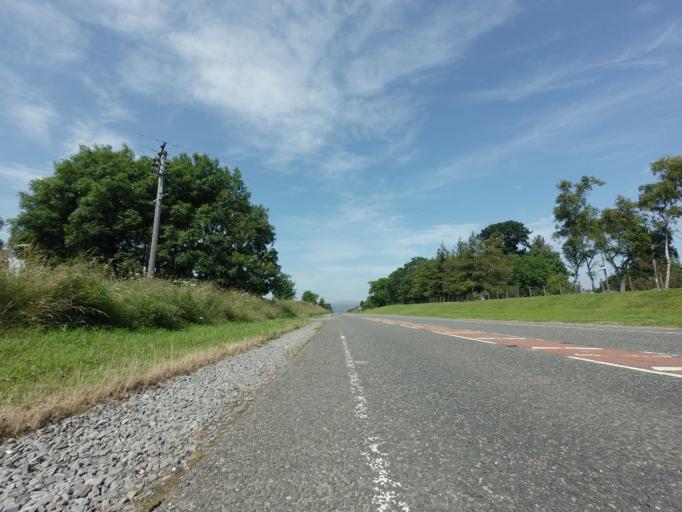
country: GB
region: Scotland
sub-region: Highland
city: Tain
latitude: 57.8241
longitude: -4.0784
